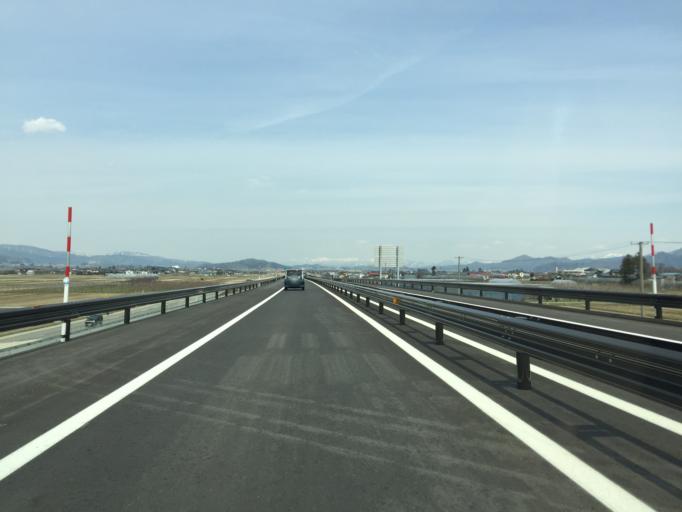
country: JP
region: Yamagata
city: Higashine
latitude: 38.4270
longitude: 140.3526
